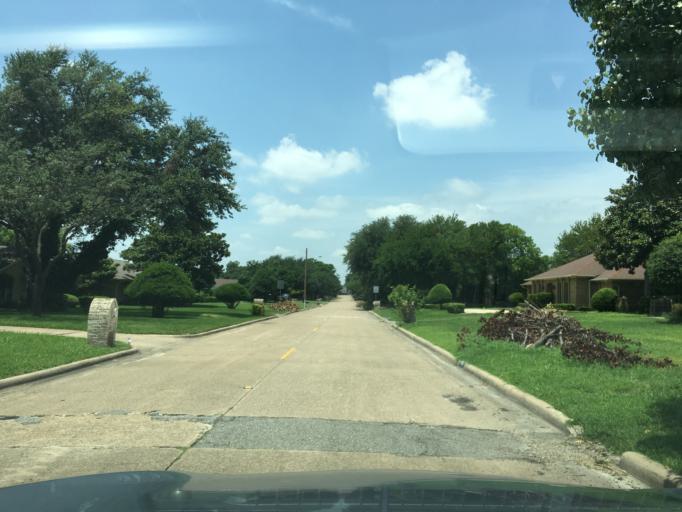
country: US
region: Texas
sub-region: Dallas County
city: Addison
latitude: 32.9216
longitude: -96.8066
